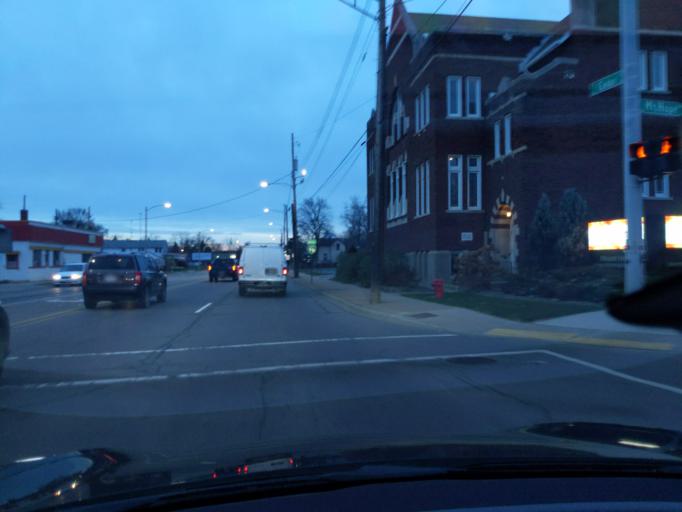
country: US
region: Michigan
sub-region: Ingham County
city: Lansing
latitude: 42.7120
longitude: -84.5477
